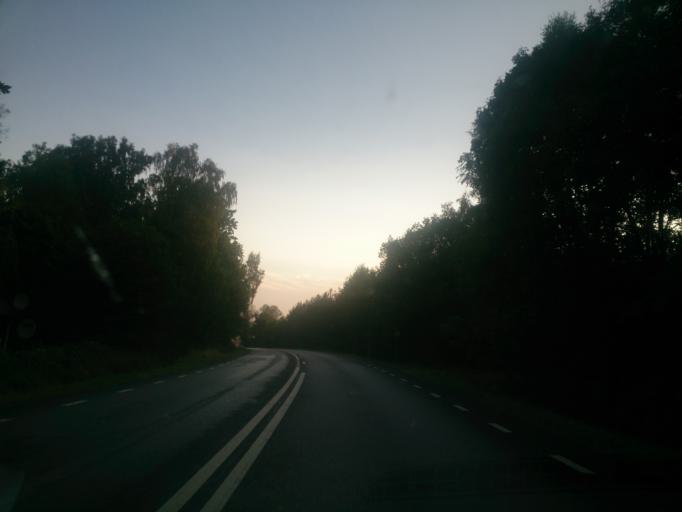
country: SE
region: Soedermanland
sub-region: Nykopings Kommun
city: Nykoping
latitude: 58.7903
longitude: 17.0765
